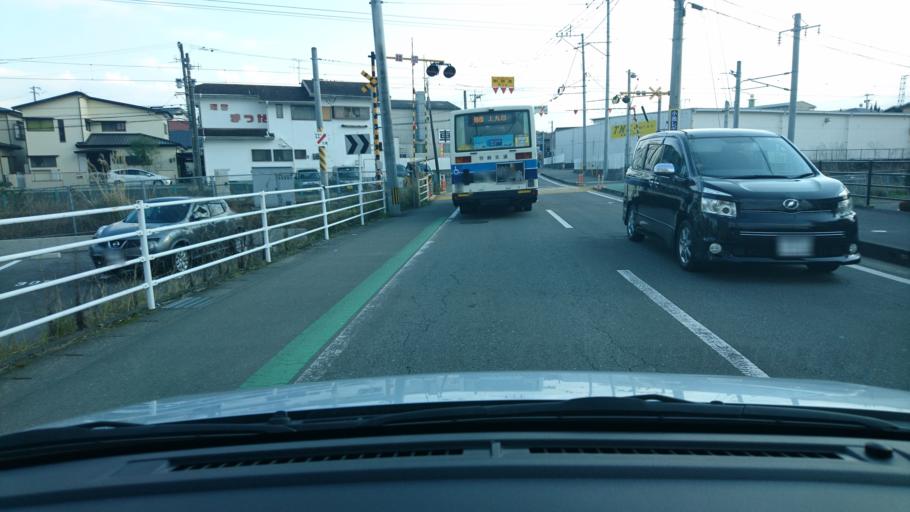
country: JP
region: Miyazaki
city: Miyazaki-shi
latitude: 31.8757
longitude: 131.4051
